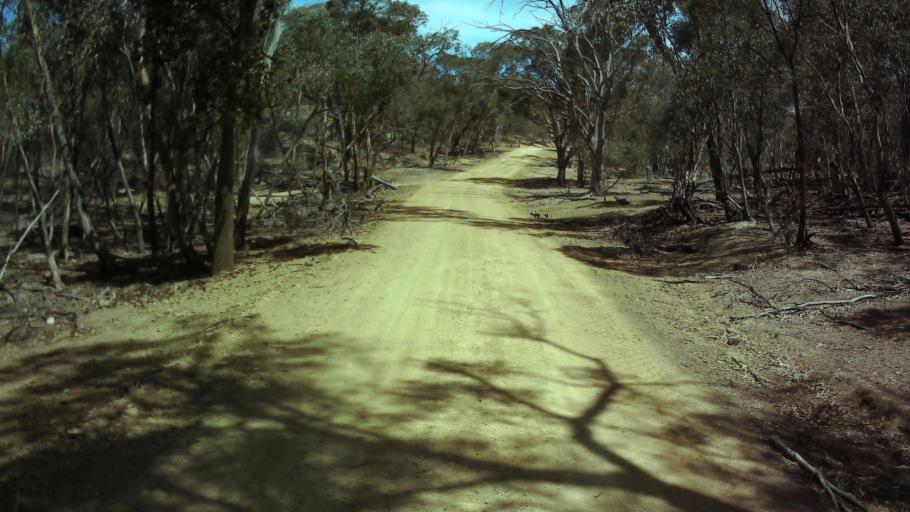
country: AU
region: New South Wales
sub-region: Weddin
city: Grenfell
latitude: -33.8038
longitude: 148.1604
